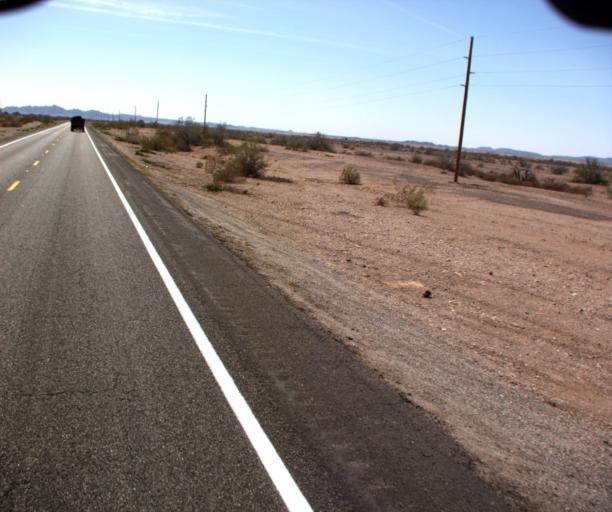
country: US
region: Arizona
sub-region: Yuma County
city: Fortuna Foothills
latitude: 32.9102
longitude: -114.3269
